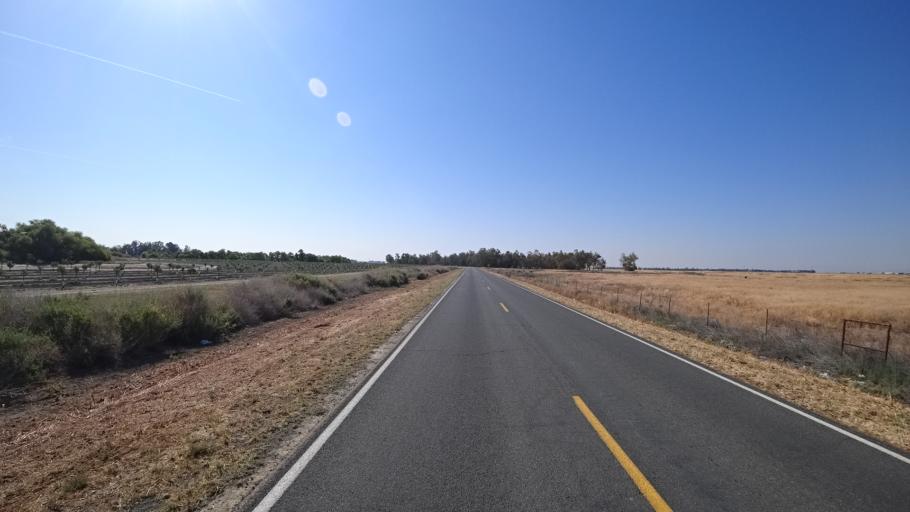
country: US
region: California
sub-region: Fresno County
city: Riverdale
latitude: 36.3655
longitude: -119.9176
